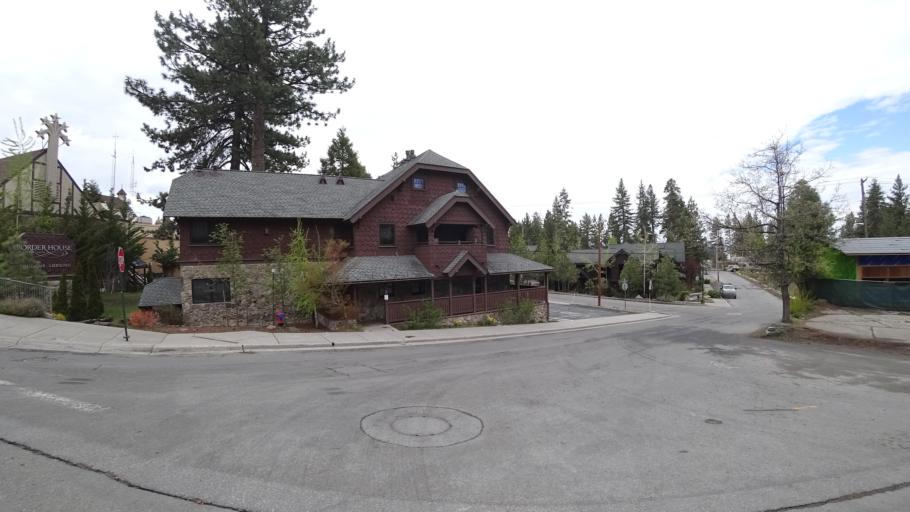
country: US
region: California
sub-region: Placer County
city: Kings Beach
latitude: 39.2274
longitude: -120.0056
